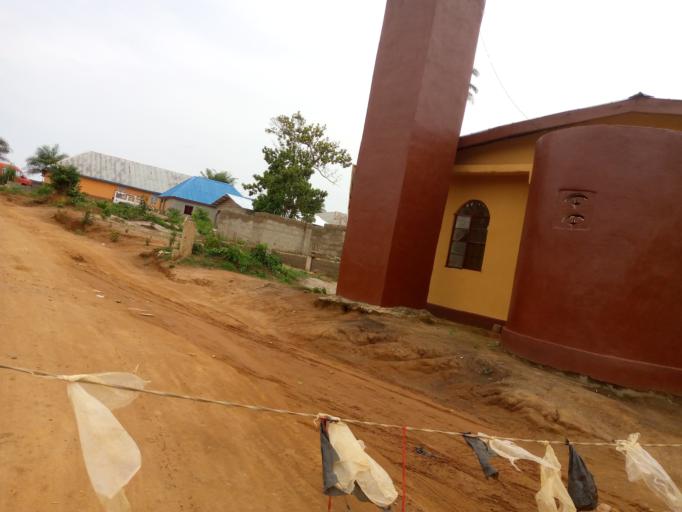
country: SL
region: Western Area
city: Waterloo
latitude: 8.3375
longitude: -13.0178
